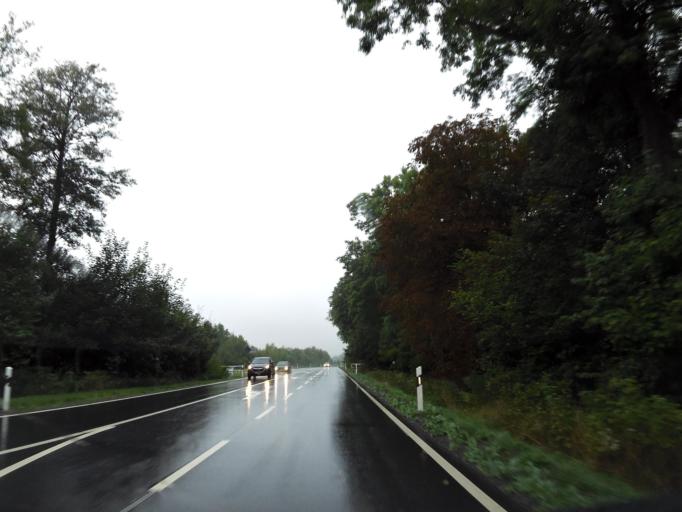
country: DE
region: Lower Saxony
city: Walkenried
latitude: 51.5927
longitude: 10.6118
